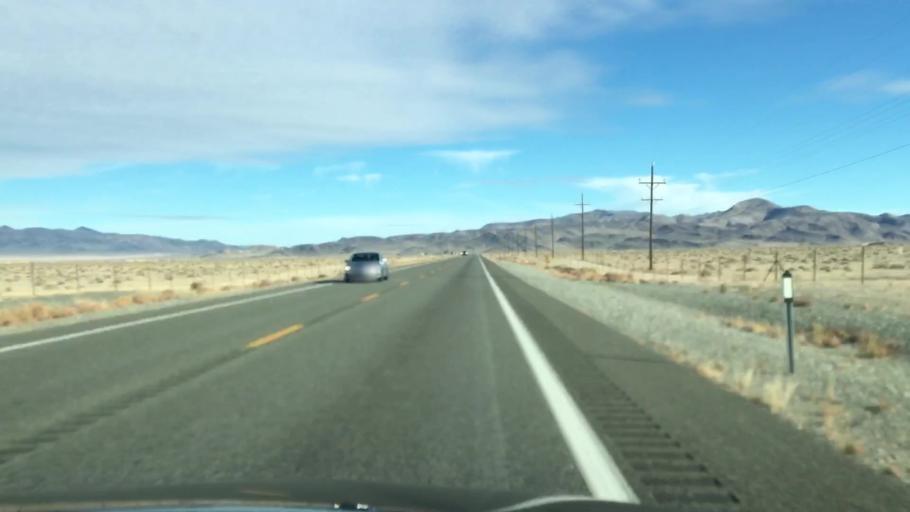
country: US
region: Nevada
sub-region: Mineral County
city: Hawthorne
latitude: 38.5246
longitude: -118.5860
